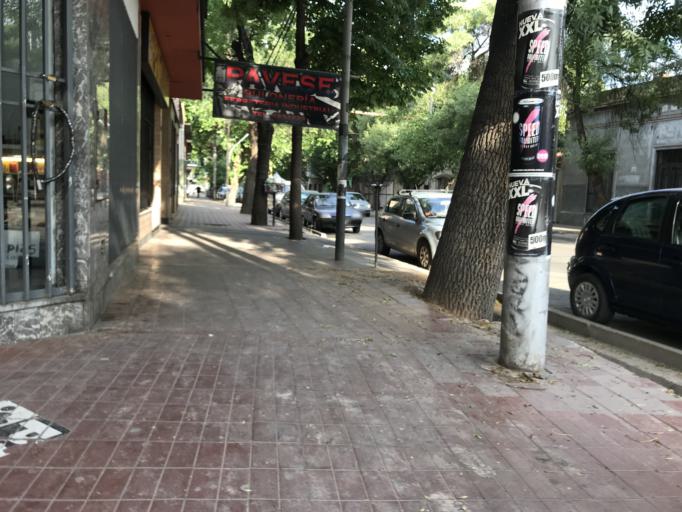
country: AR
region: Mendoza
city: Mendoza
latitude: -32.8785
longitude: -68.8375
